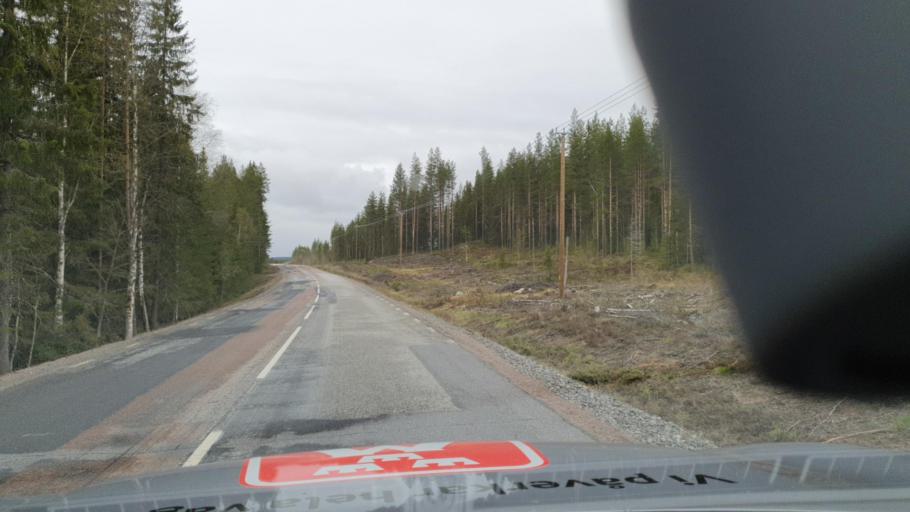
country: SE
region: Vaesternorrland
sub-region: Solleftea Kommun
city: Solleftea
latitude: 63.6302
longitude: 17.4414
